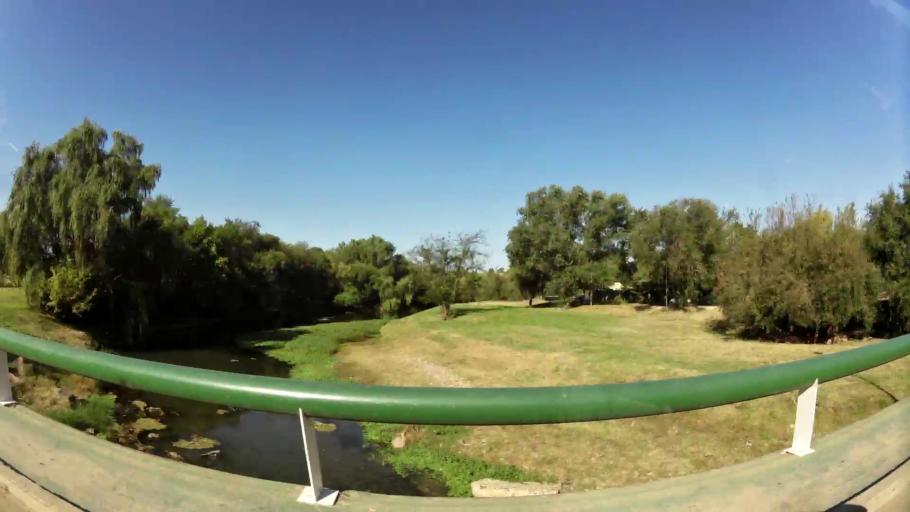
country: AR
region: Cordoba
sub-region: Departamento de Capital
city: Cordoba
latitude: -31.3750
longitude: -64.2488
